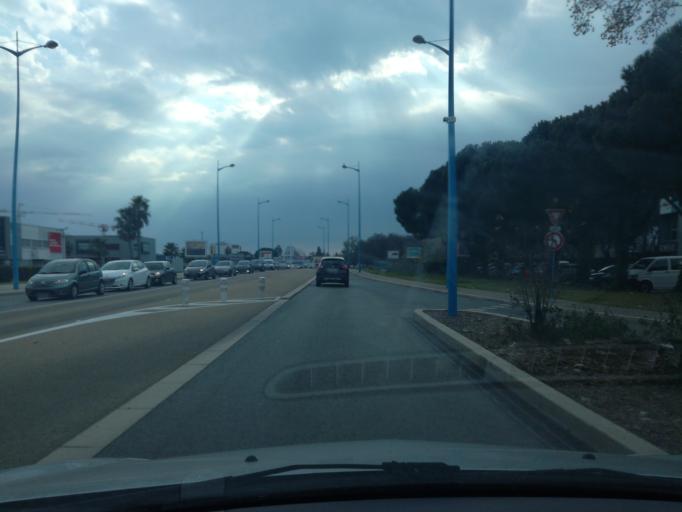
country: FR
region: Provence-Alpes-Cote d'Azur
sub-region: Departement des Alpes-Maritimes
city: Mandelieu-la-Napoule
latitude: 43.5543
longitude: 6.9545
